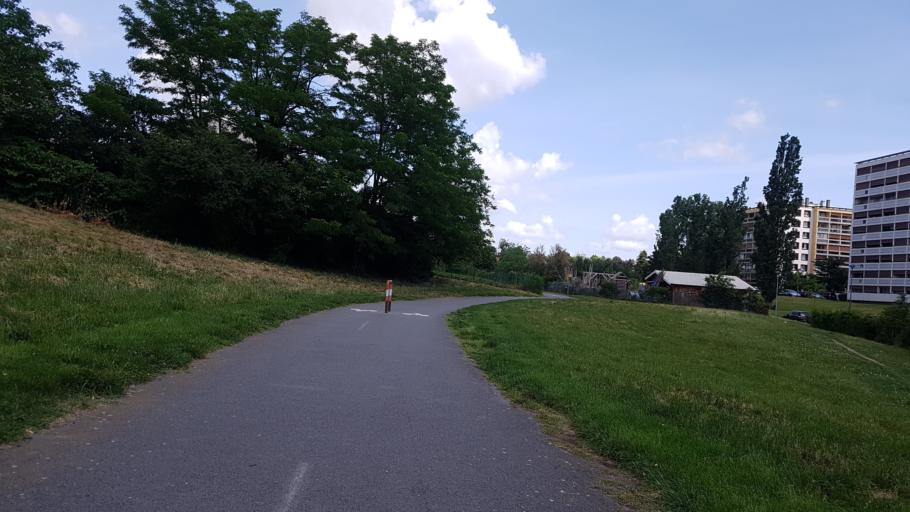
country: FR
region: Rhone-Alpes
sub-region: Departement du Rhone
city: Rillieux-la-Pape
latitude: 45.8207
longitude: 4.9042
